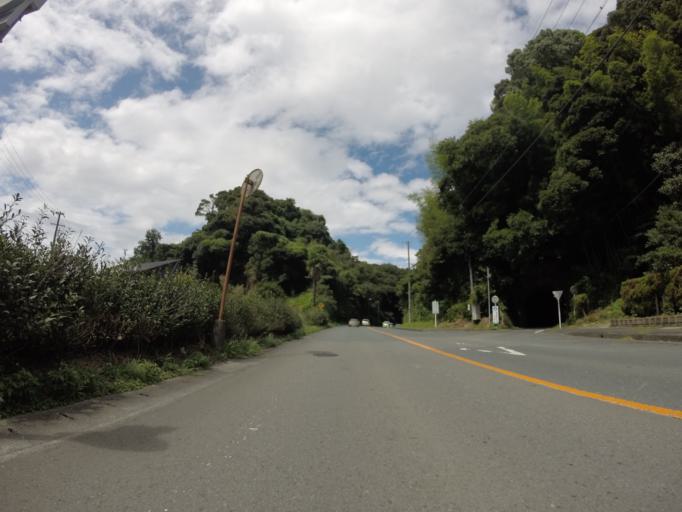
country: JP
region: Shizuoka
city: Kakegawa
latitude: 34.7432
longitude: 138.0397
